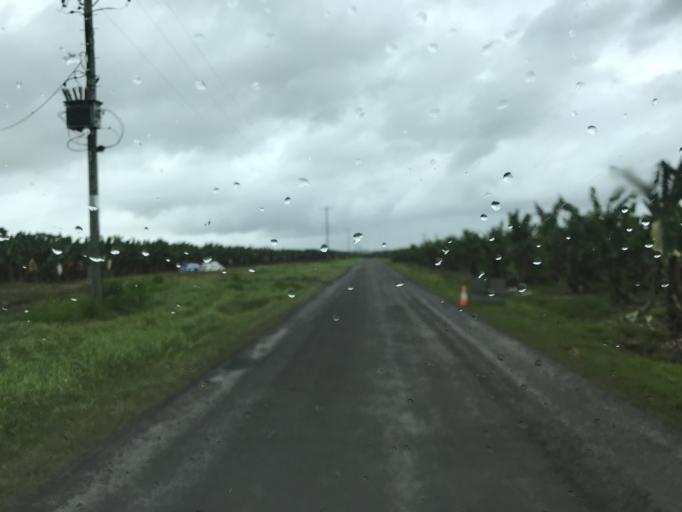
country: AU
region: Queensland
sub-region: Cassowary Coast
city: Innisfail
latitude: -17.5057
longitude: 145.9794
